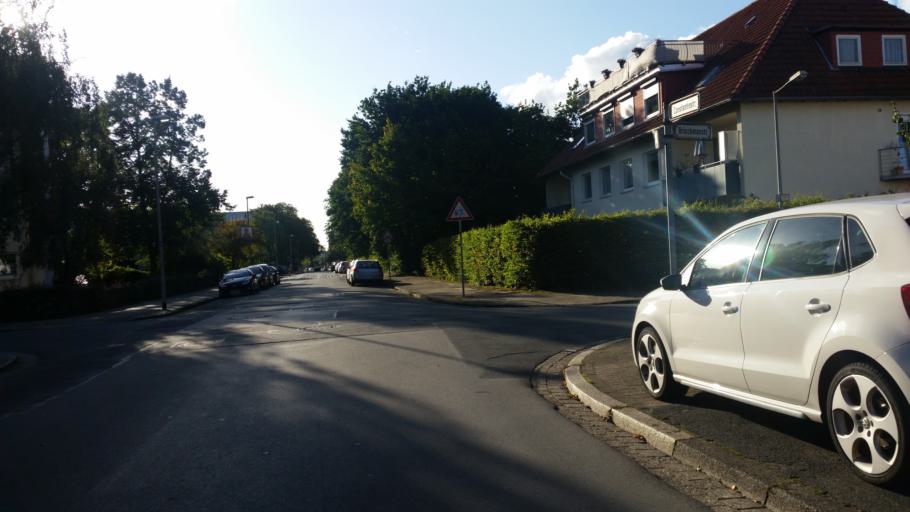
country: DE
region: Lower Saxony
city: Hannover
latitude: 52.4020
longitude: 9.7708
